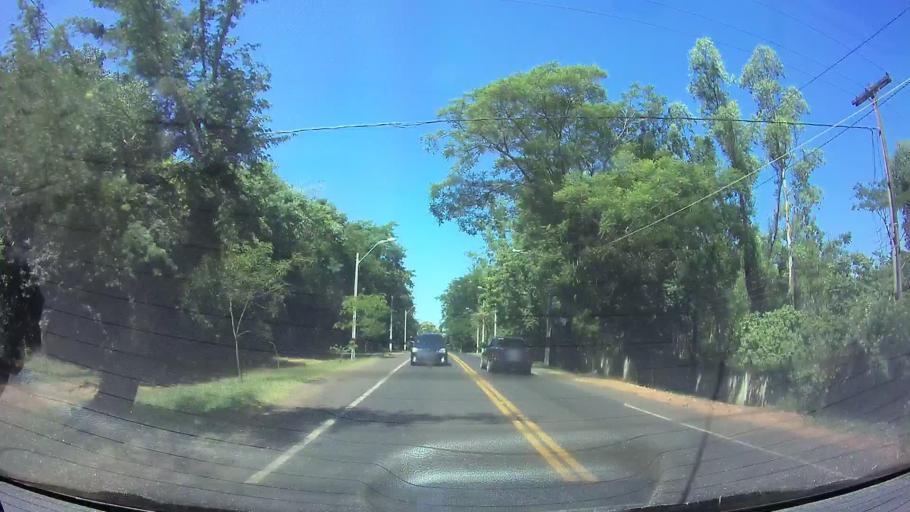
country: PY
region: Central
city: Aregua
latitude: -25.3272
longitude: -57.3972
